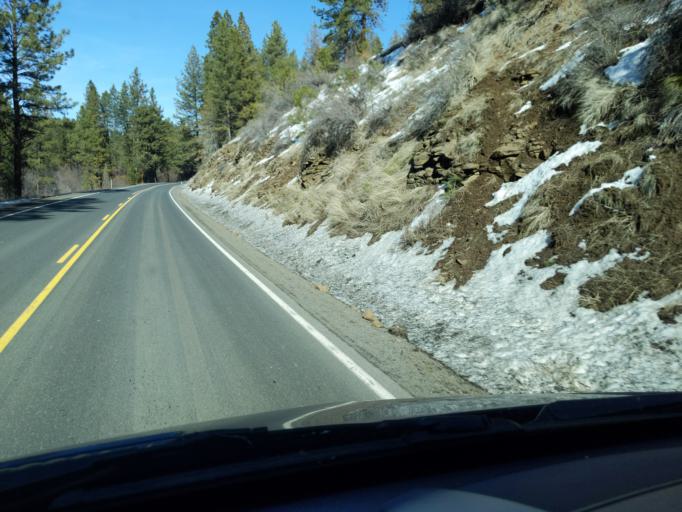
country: US
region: Oregon
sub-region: Grant County
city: John Day
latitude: 44.8709
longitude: -119.0217
